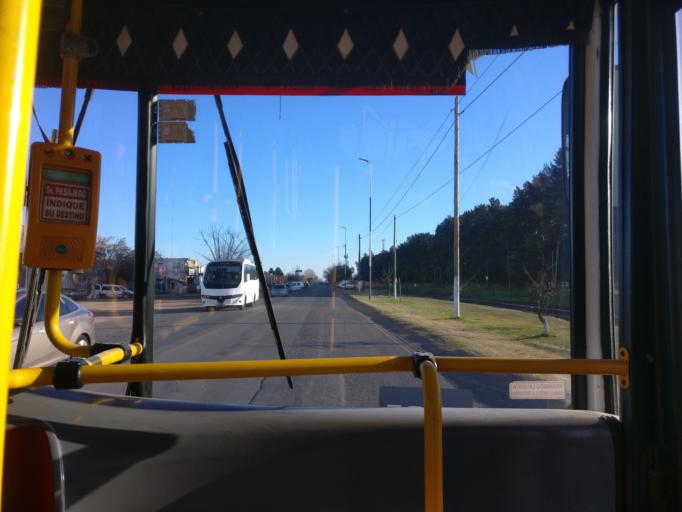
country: AR
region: Buenos Aires
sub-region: Partido de Ezeiza
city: Ezeiza
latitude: -34.8979
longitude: -58.5784
